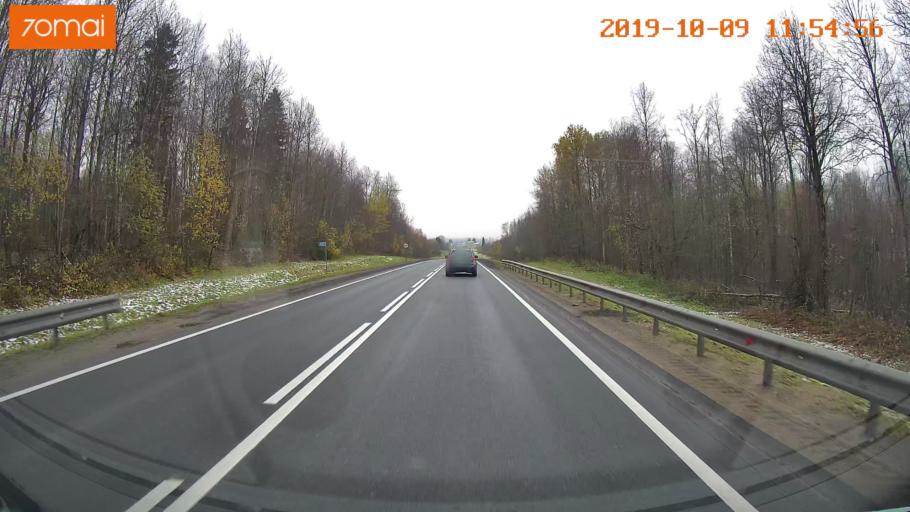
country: RU
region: Vologda
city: Gryazovets
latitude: 58.7532
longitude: 40.2838
